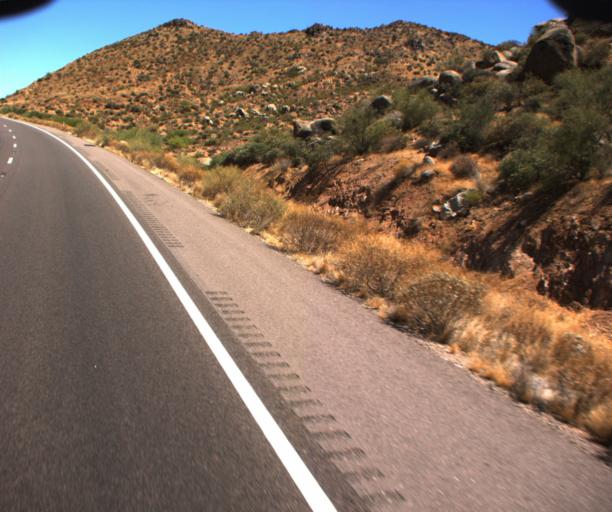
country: US
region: Arizona
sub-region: Maricopa County
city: Rio Verde
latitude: 33.7117
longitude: -111.5095
